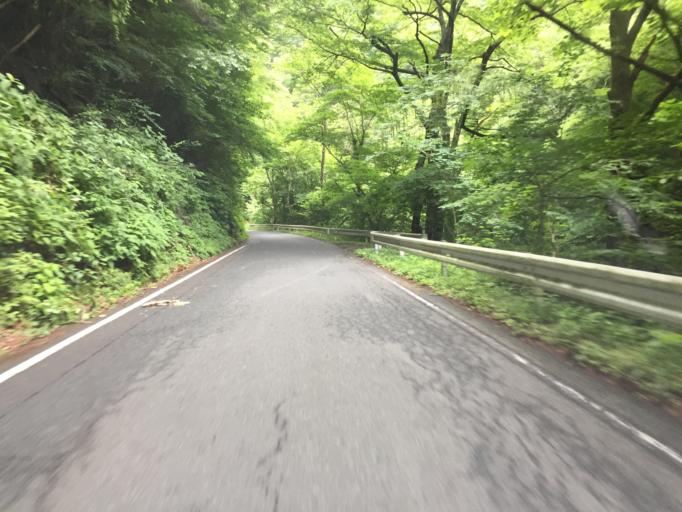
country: JP
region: Fukushima
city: Namie
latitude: 37.6895
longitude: 140.8788
